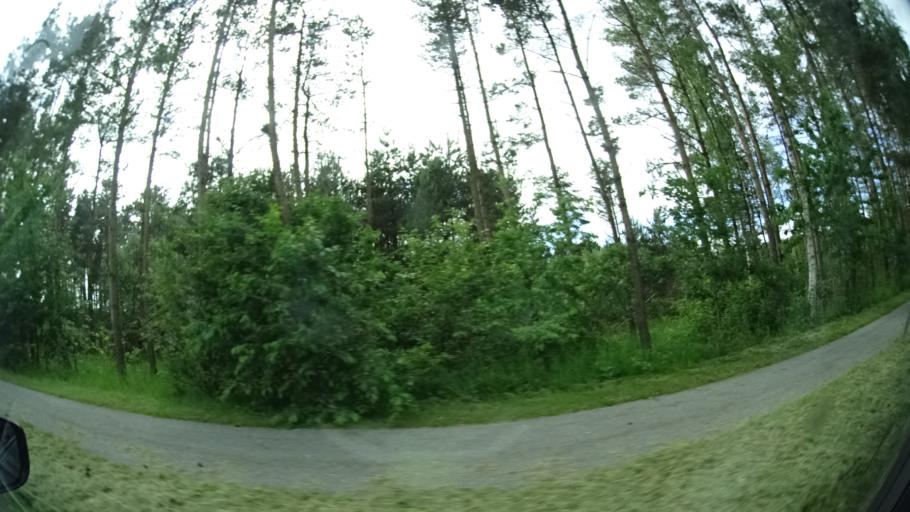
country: DK
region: Central Jutland
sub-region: Norddjurs Kommune
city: Grenaa
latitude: 56.4841
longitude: 10.7311
